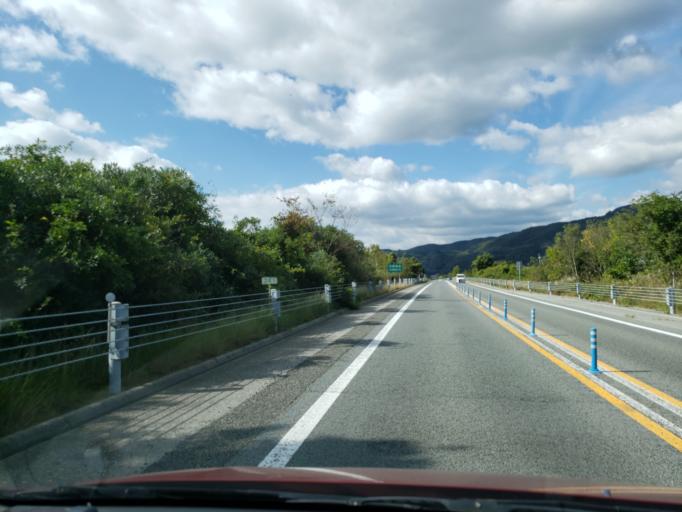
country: JP
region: Tokushima
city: Kamojimacho-jogejima
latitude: 34.1185
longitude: 134.3378
